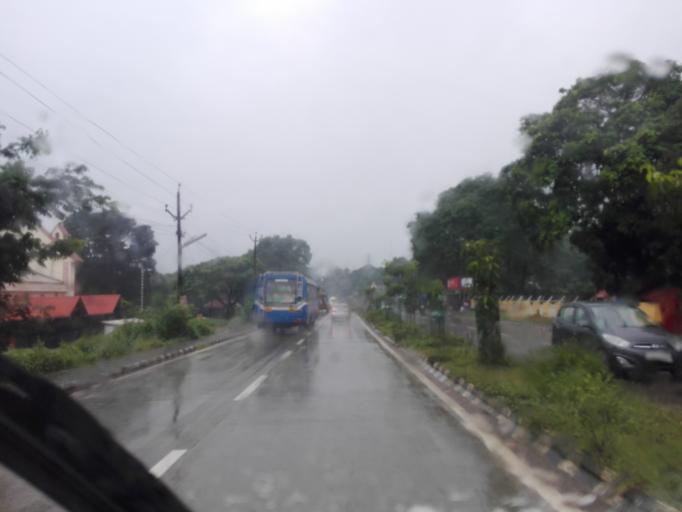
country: IN
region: Kerala
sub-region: Ernakulam
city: Elur
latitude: 10.0527
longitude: 76.3326
